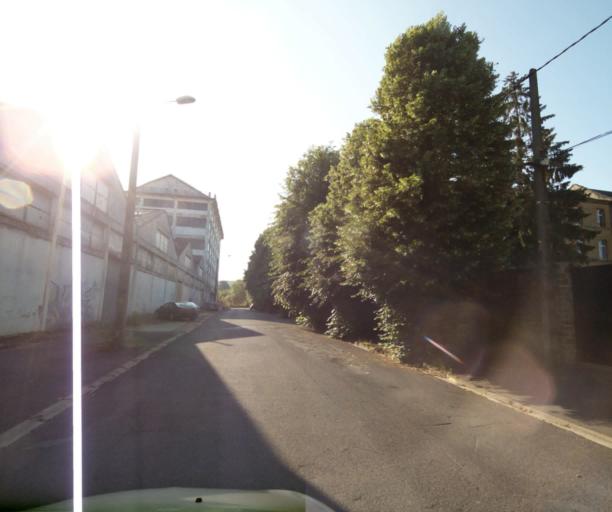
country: FR
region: Champagne-Ardenne
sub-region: Departement des Ardennes
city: Montcy-Notre-Dame
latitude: 49.7744
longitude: 4.7294
